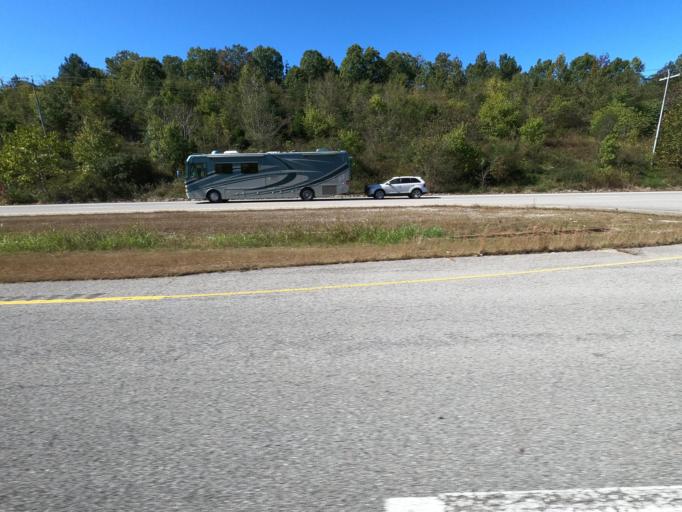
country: US
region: Tennessee
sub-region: Maury County
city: Mount Pleasant
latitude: 35.4672
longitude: -87.2657
